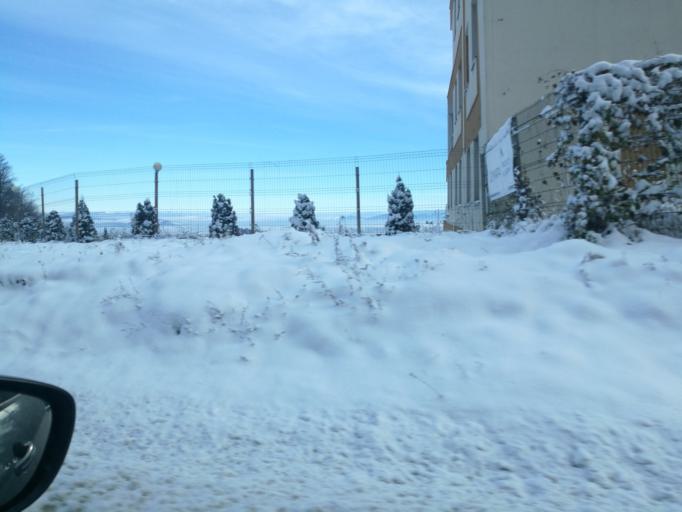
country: RO
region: Brasov
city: Brasov
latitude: 45.6387
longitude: 25.5633
